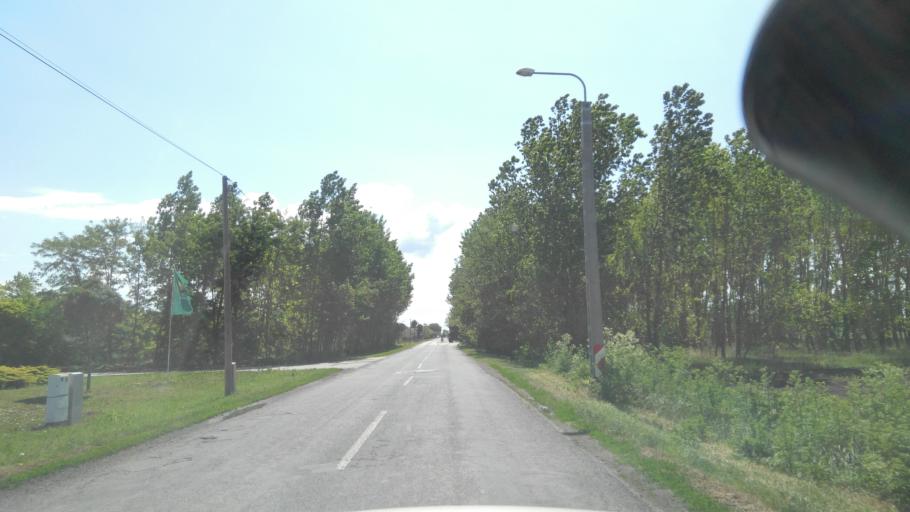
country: HU
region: Bekes
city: Kunagota
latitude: 46.4232
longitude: 21.0265
